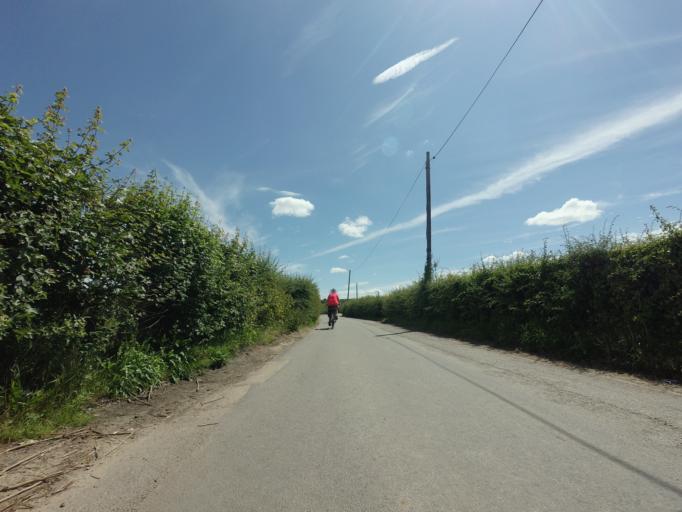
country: GB
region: England
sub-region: Medway
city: Cooling
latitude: 51.4574
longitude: 0.5364
